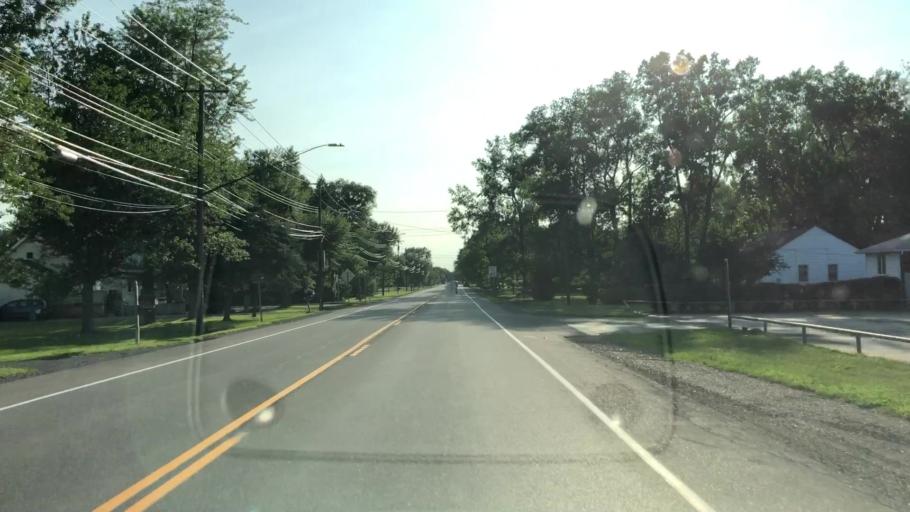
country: US
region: New York
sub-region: Erie County
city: Cheektowaga
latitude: 42.8569
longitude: -78.7344
